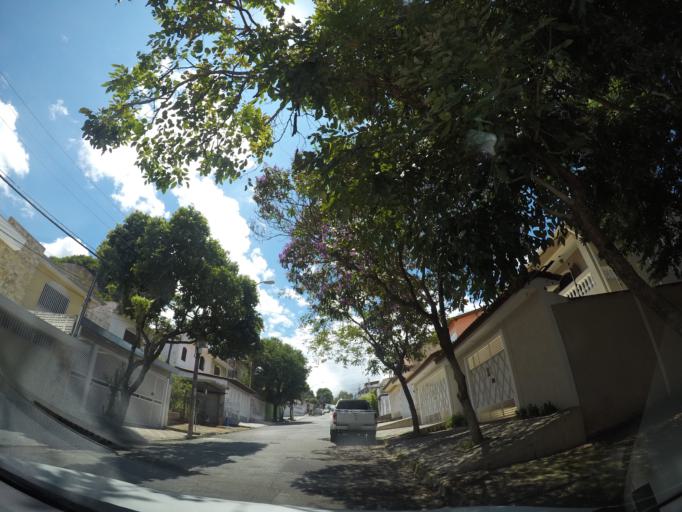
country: BR
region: Sao Paulo
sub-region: Guarulhos
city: Guarulhos
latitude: -23.4516
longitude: -46.5392
